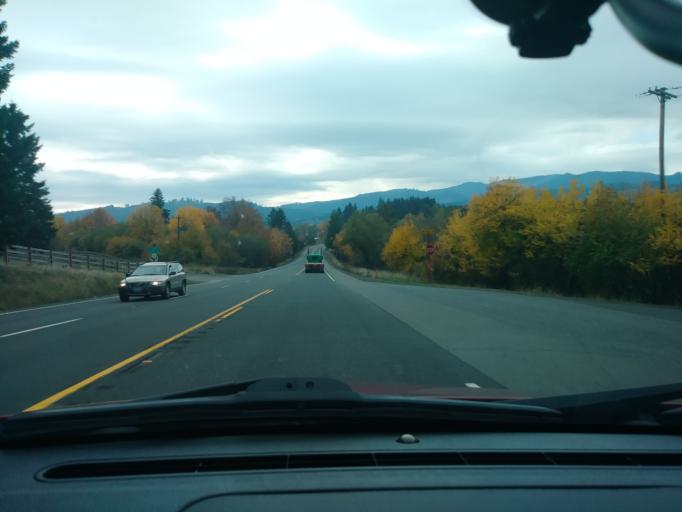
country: US
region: Oregon
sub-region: Washington County
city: Banks
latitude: 45.6143
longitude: -123.2272
